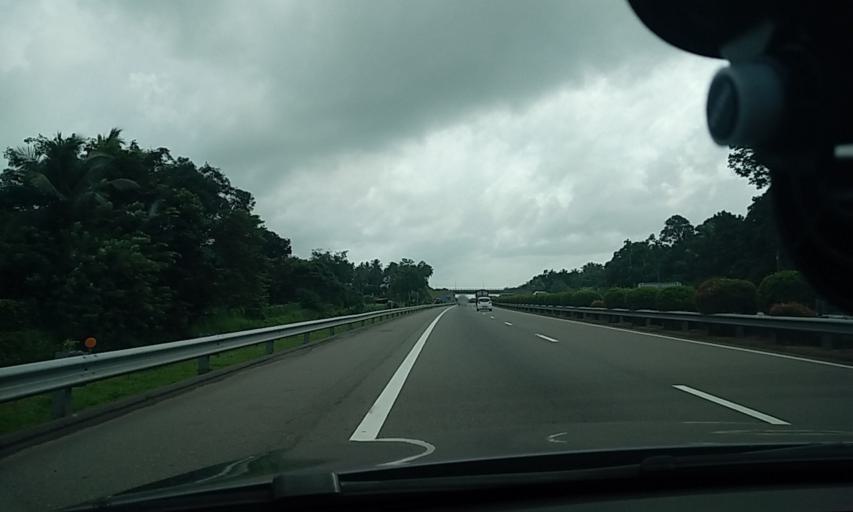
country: LK
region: Western
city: Homagama
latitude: 6.8598
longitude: 79.9777
